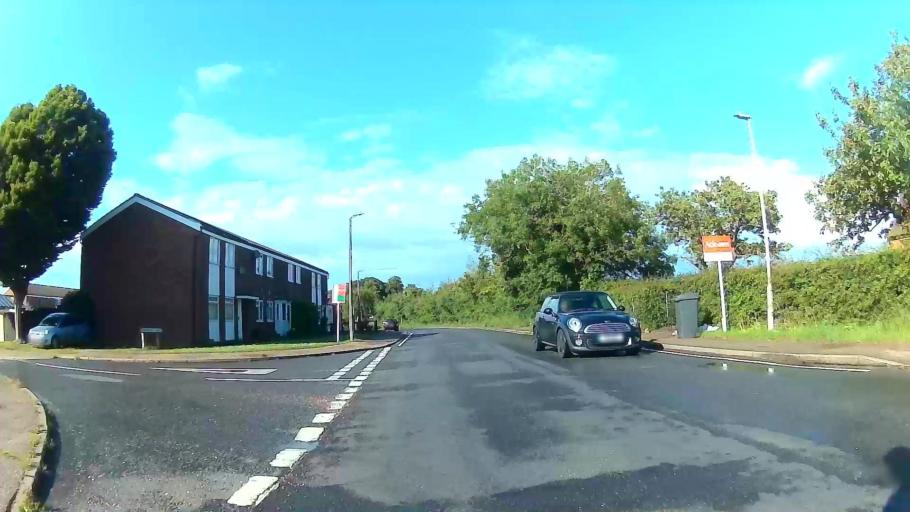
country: GB
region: England
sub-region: Essex
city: Ingatestone
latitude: 51.7123
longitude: 0.3770
